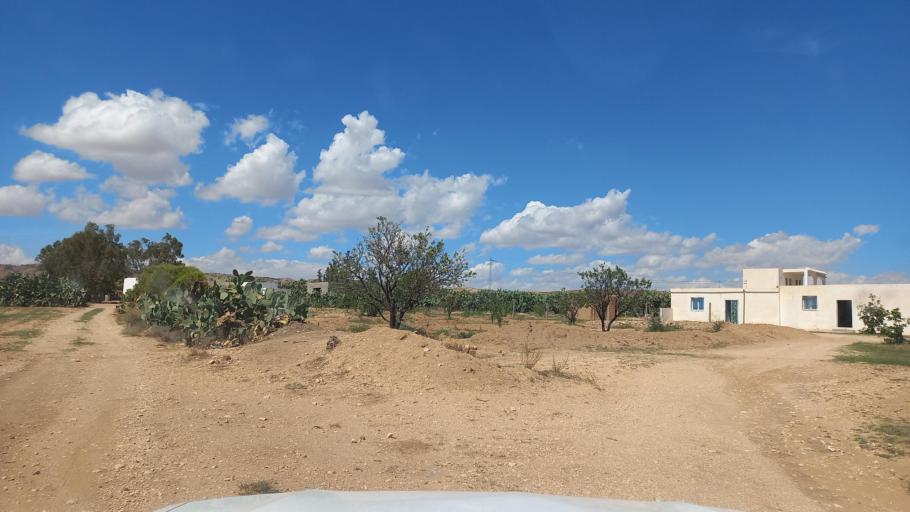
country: TN
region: Al Qasrayn
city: Sbiba
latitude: 35.3455
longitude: 9.0099
